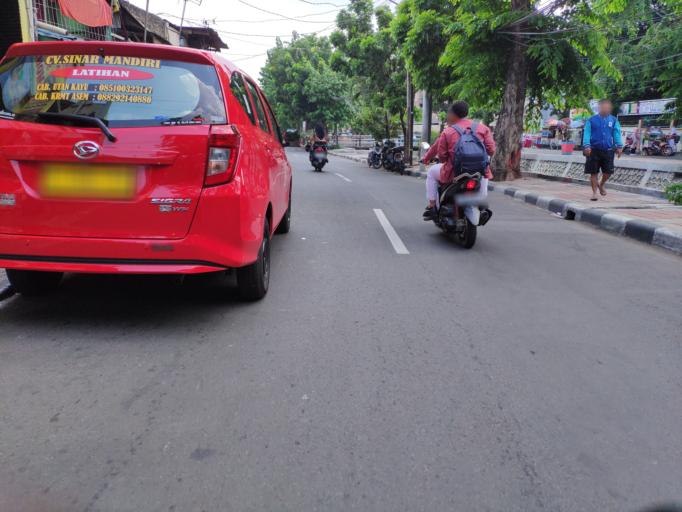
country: ID
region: Jakarta Raya
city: Jakarta
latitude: -6.1960
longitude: 106.8684
